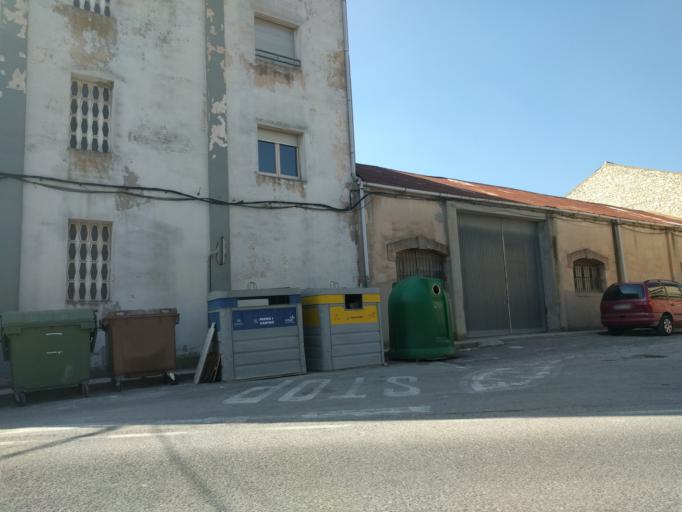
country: ES
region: Catalonia
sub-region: Provincia de Tarragona
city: Santa Coloma de Queralt
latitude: 41.5306
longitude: 1.3797
